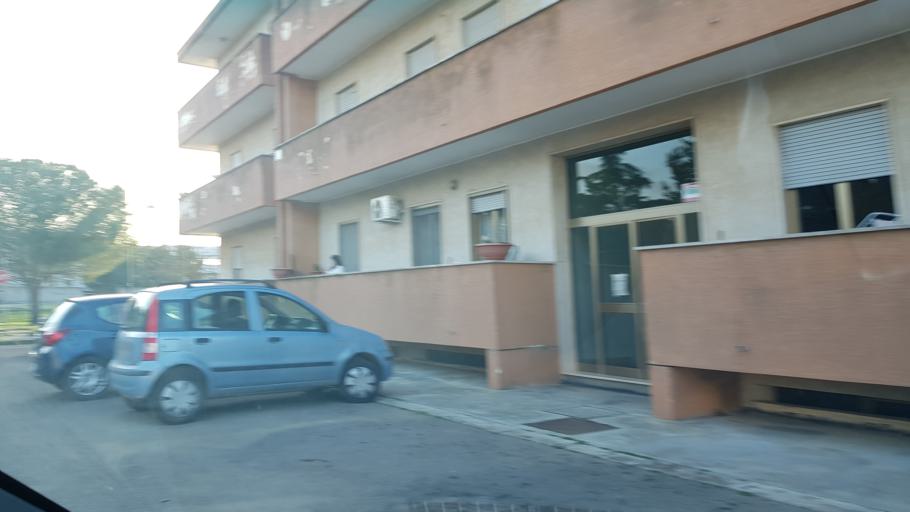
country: IT
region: Apulia
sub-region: Provincia di Lecce
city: Campi Salentina
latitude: 40.4047
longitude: 18.0152
